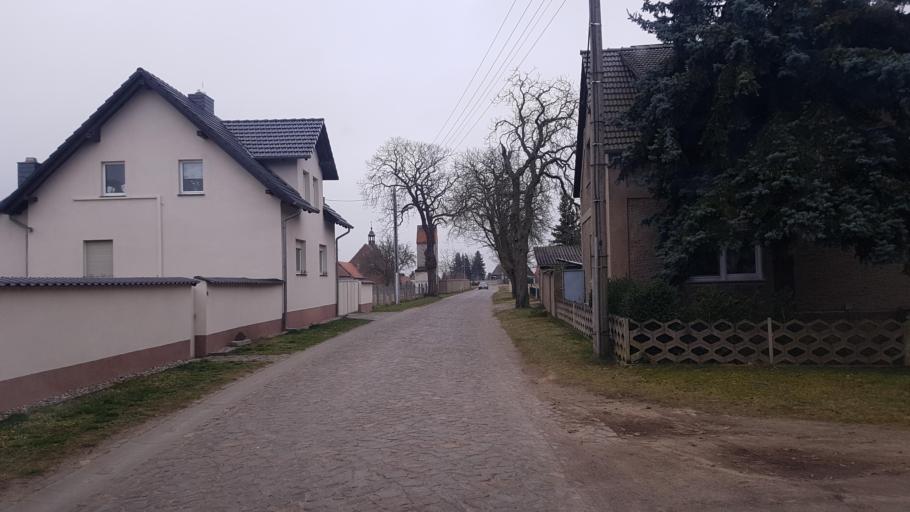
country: DE
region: Brandenburg
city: Herzberg
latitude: 51.6789
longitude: 13.1720
